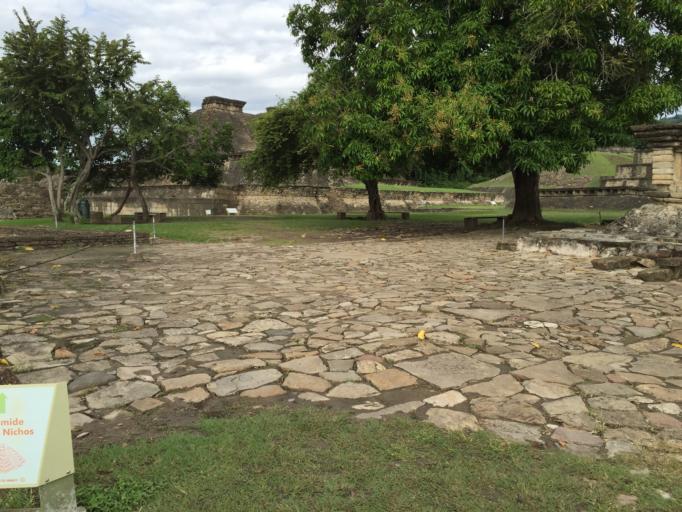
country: MX
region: Veracruz
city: Papantla de Olarte
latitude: 20.4471
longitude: -97.3773
